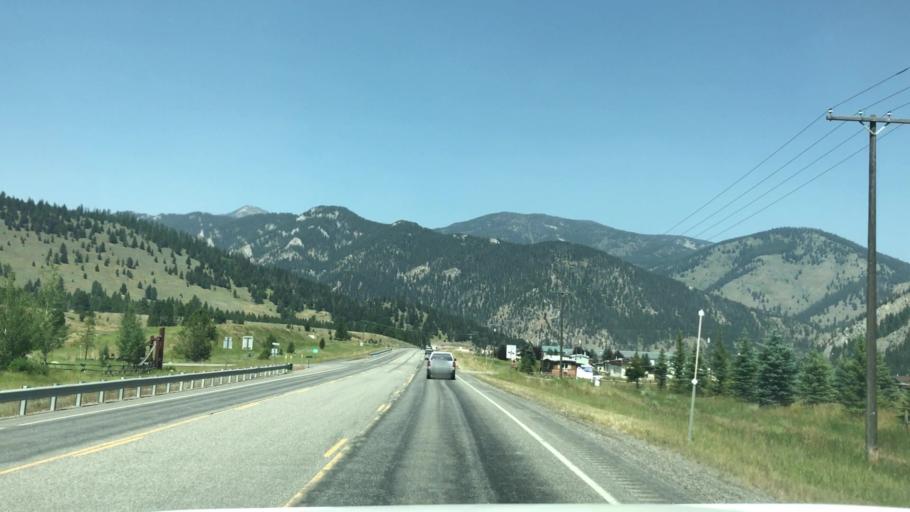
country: US
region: Montana
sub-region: Gallatin County
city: Big Sky
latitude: 45.2487
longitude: -111.2520
